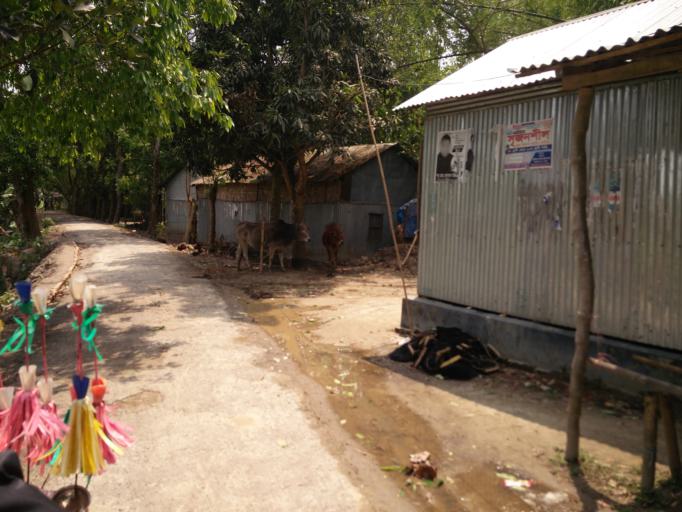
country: BD
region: Dhaka
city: Sherpur
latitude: 24.9352
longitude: 90.1590
